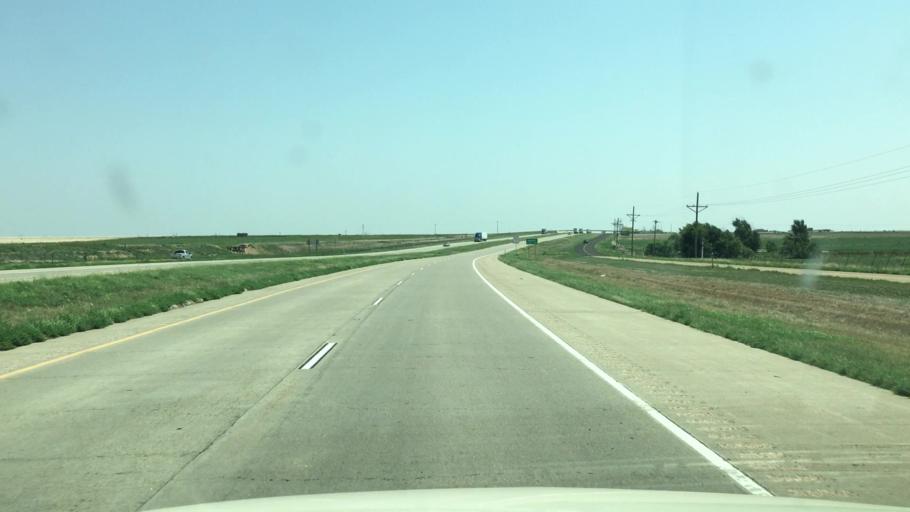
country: US
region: Texas
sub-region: Potter County
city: Bushland
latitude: 35.2087
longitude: -102.1693
